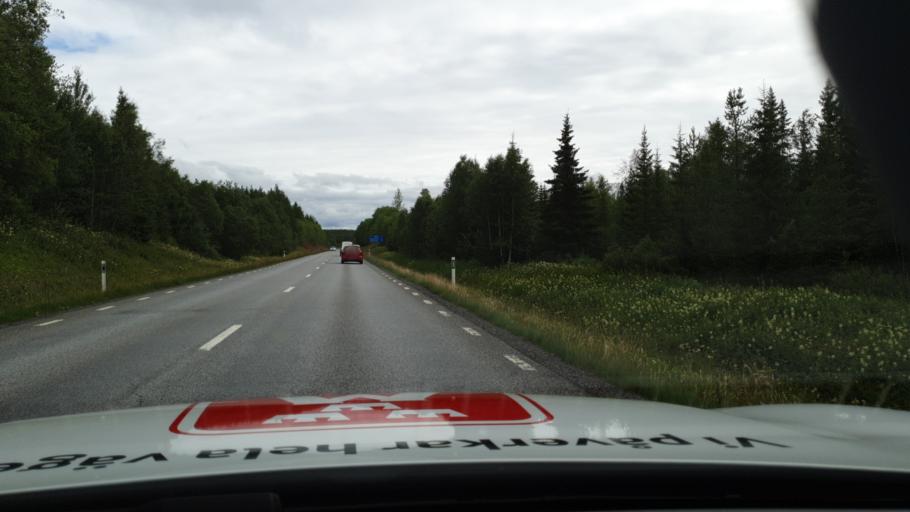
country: SE
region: Jaemtland
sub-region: OEstersunds Kommun
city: Lit
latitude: 63.4438
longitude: 15.1405
